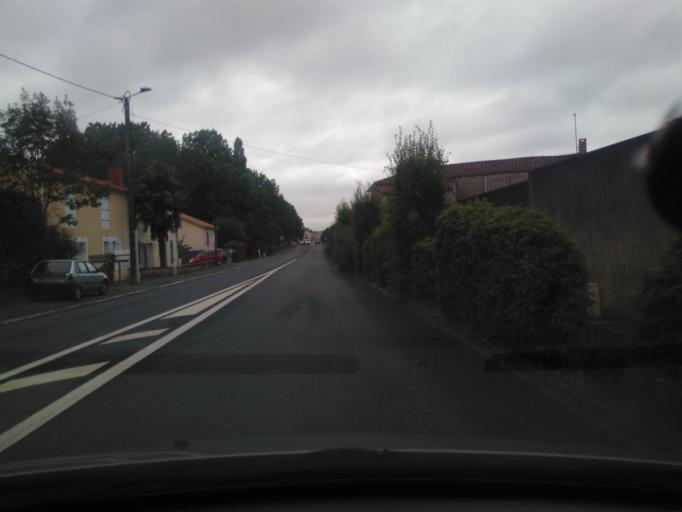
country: FR
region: Pays de la Loire
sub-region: Departement de la Vendee
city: Mareuil-sur-Lay-Dissais
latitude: 46.5376
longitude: -1.2289
